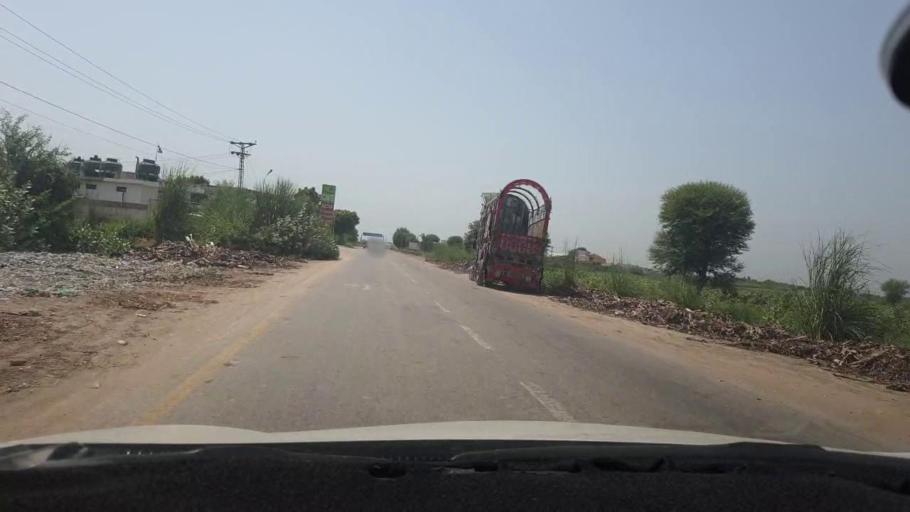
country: PK
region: Sindh
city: Shahdadpur
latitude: 25.9112
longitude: 68.6044
